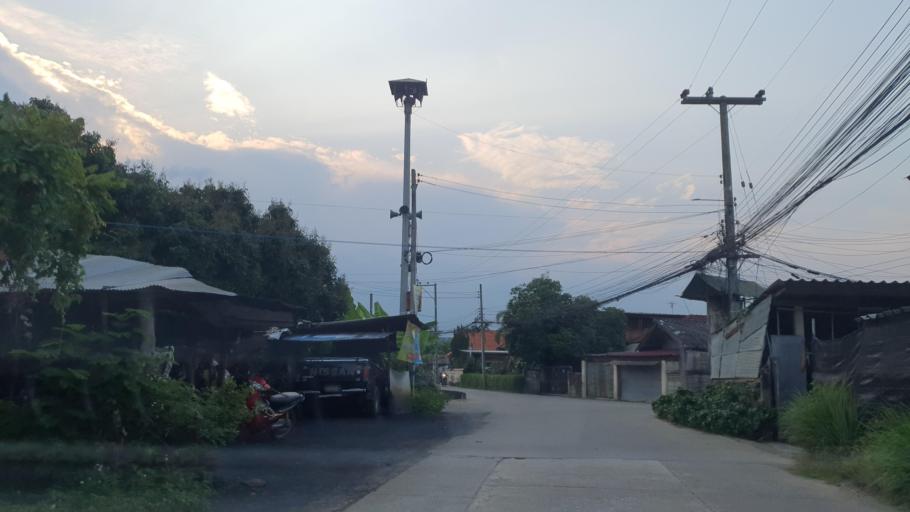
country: TH
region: Chiang Mai
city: Hang Dong
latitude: 18.6657
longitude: 98.9302
